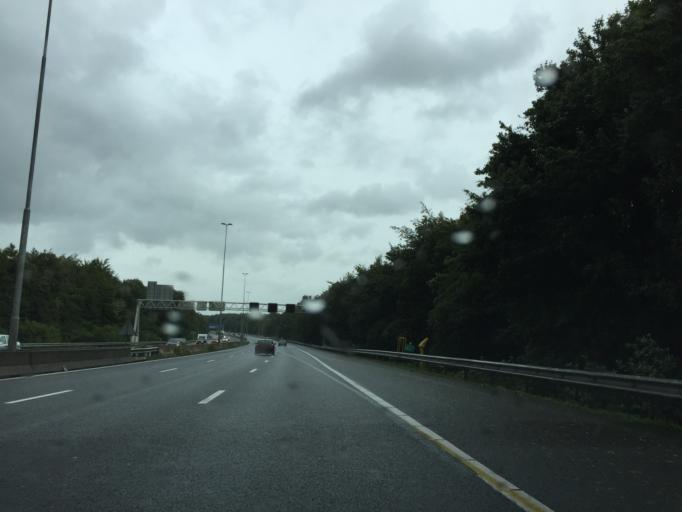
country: NL
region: North Holland
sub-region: Gemeente Amstelveen
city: Amstelveen
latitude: 52.3110
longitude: 4.8182
